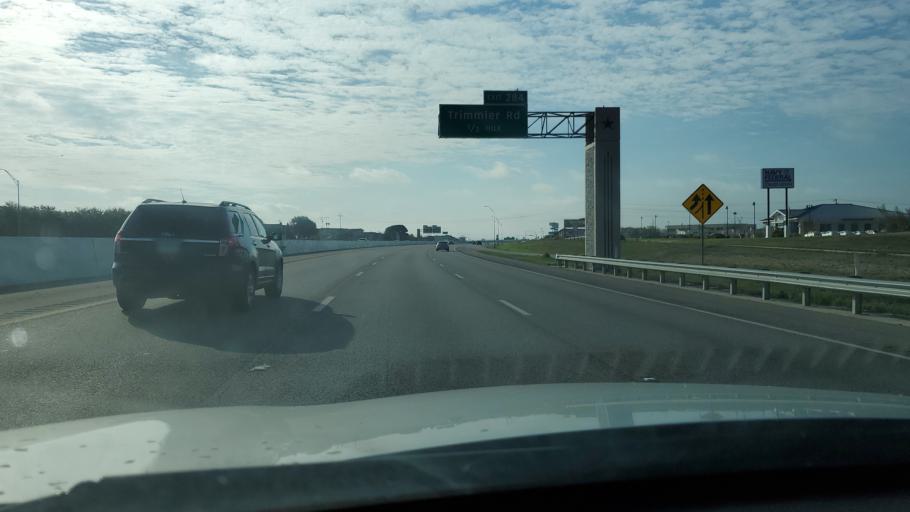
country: US
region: Texas
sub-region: Bell County
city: Killeen
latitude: 31.1073
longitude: -97.7449
